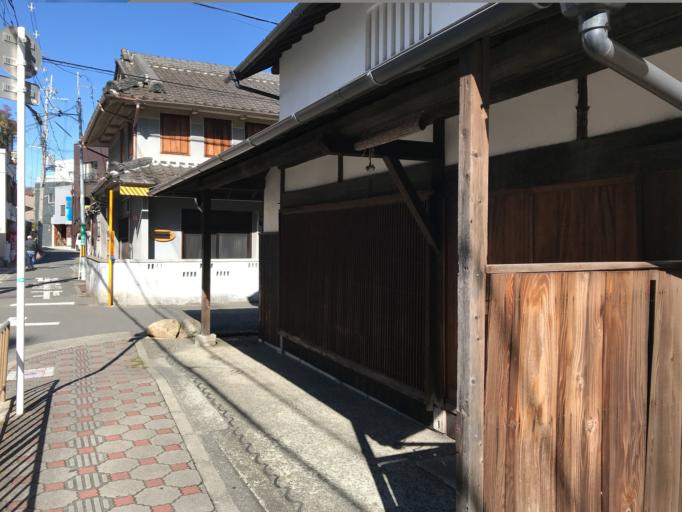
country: JP
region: Osaka
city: Tondabayashicho
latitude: 34.4519
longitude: 135.5725
